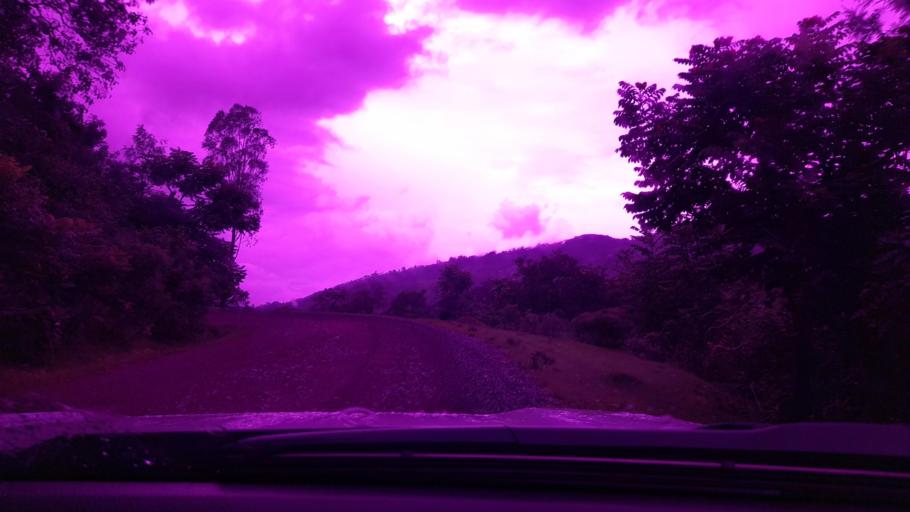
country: ET
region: Oromiya
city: Metu
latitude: 8.4410
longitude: 35.6199
